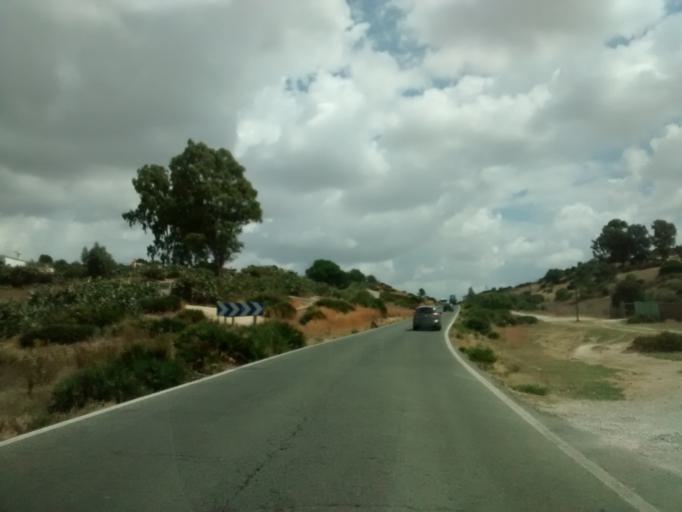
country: ES
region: Andalusia
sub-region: Provincia de Cadiz
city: Paterna de Rivera
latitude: 36.4921
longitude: -5.8954
